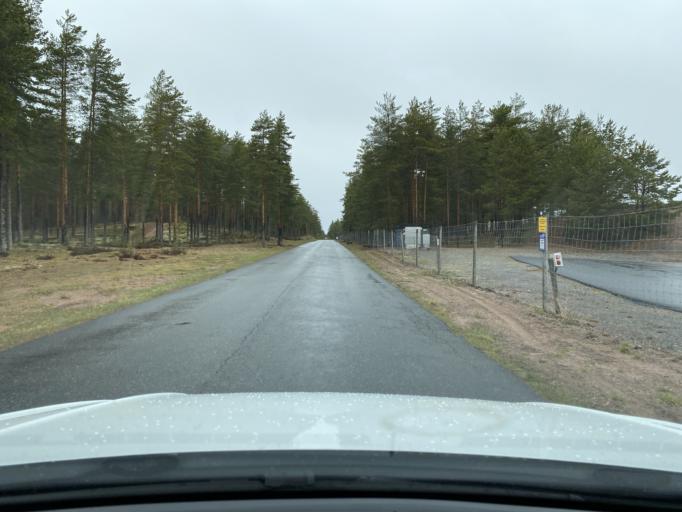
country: FI
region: Satakunta
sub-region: Pori
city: Vampula
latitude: 60.9713
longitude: 22.6580
